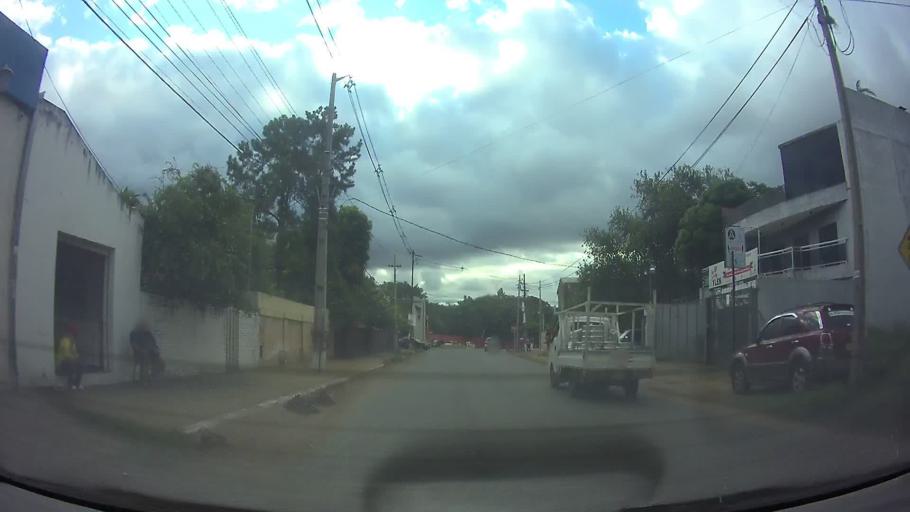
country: PY
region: Central
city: Fernando de la Mora
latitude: -25.3180
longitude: -57.5426
